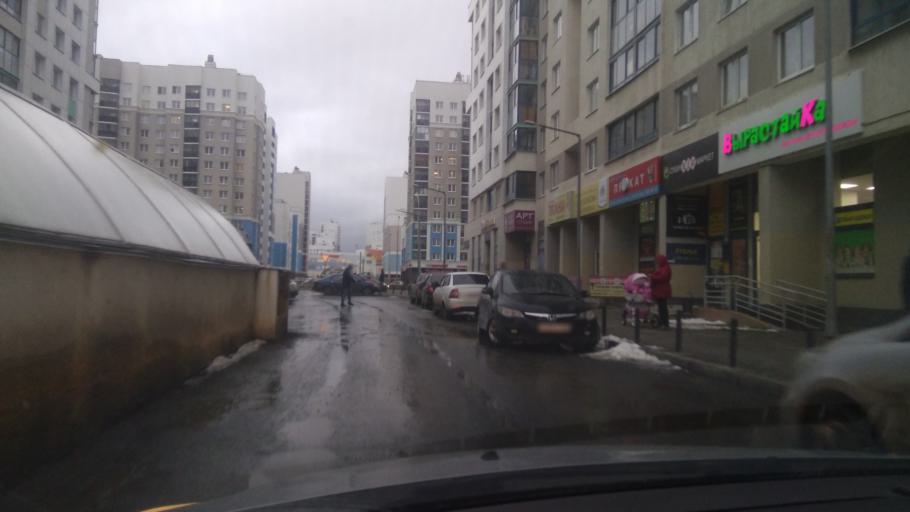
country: RU
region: Sverdlovsk
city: Shirokaya Rechka
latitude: 56.7898
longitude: 60.5180
